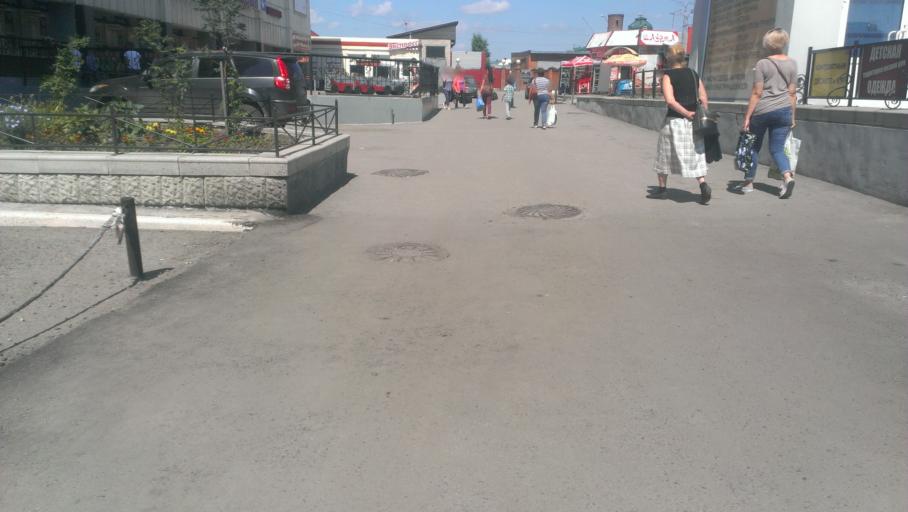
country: RU
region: Altai Krai
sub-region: Gorod Barnaulskiy
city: Barnaul
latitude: 53.3517
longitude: 83.7580
